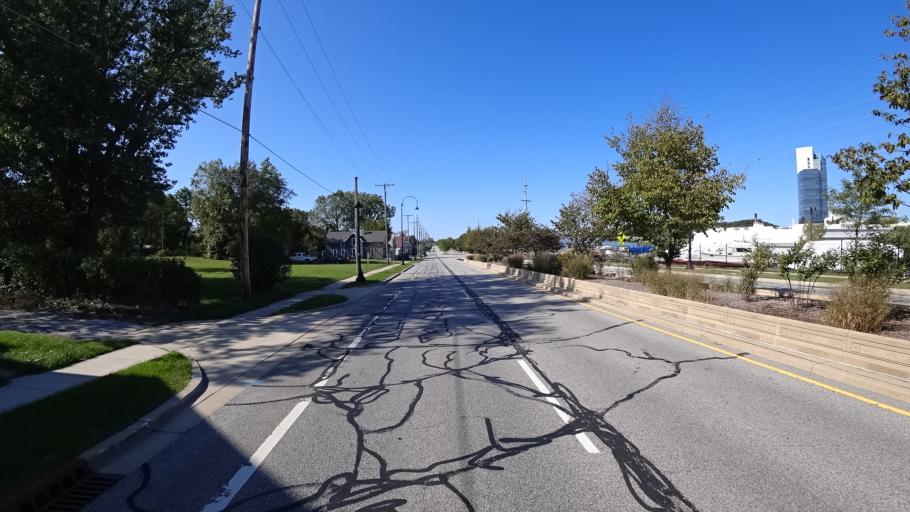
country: US
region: Indiana
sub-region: LaPorte County
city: Michigan City
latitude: 41.7161
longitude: -86.8928
